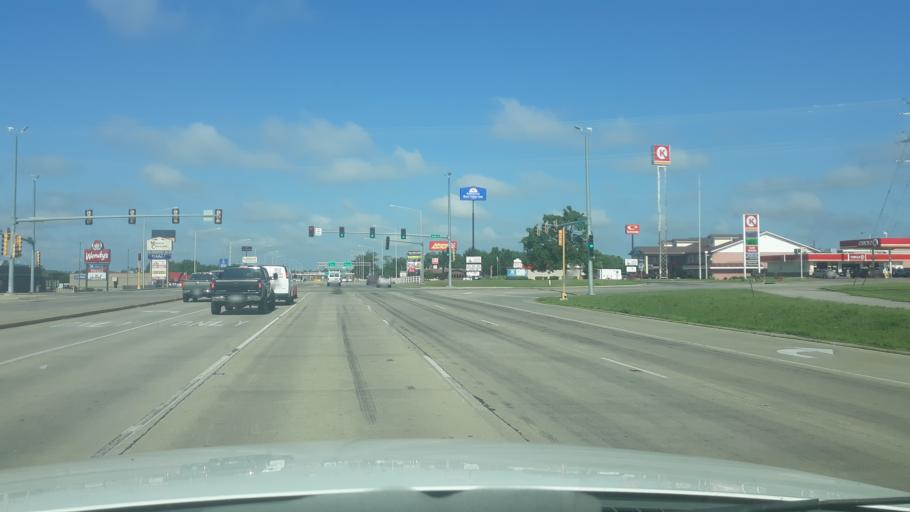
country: US
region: Illinois
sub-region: Williamson County
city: Marion
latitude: 37.7408
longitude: -88.9469
